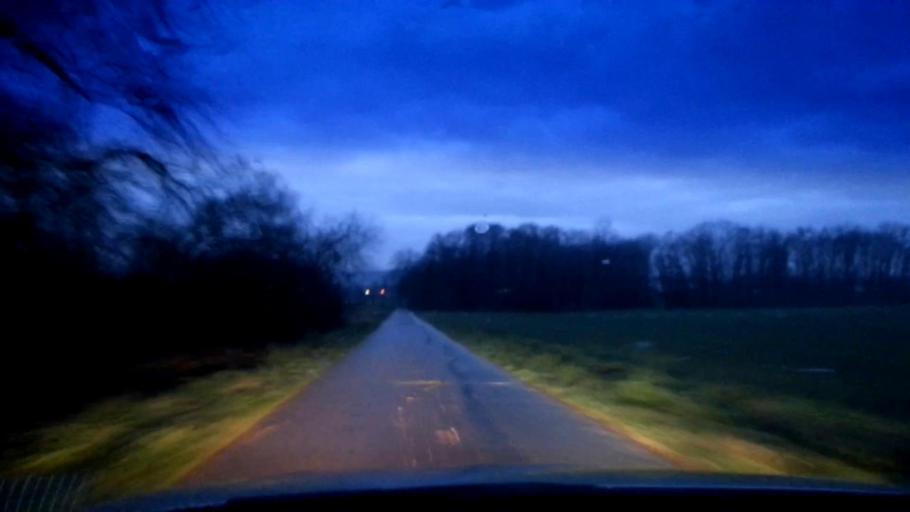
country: DE
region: Bavaria
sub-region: Upper Franconia
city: Memmelsdorf
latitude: 49.9642
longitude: 10.9638
